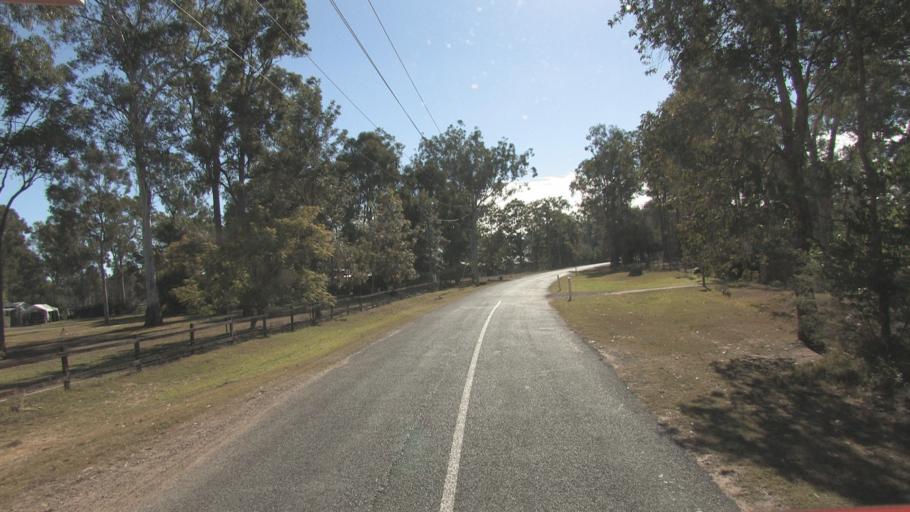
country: AU
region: Queensland
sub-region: Logan
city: Chambers Flat
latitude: -27.7910
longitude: 153.0659
